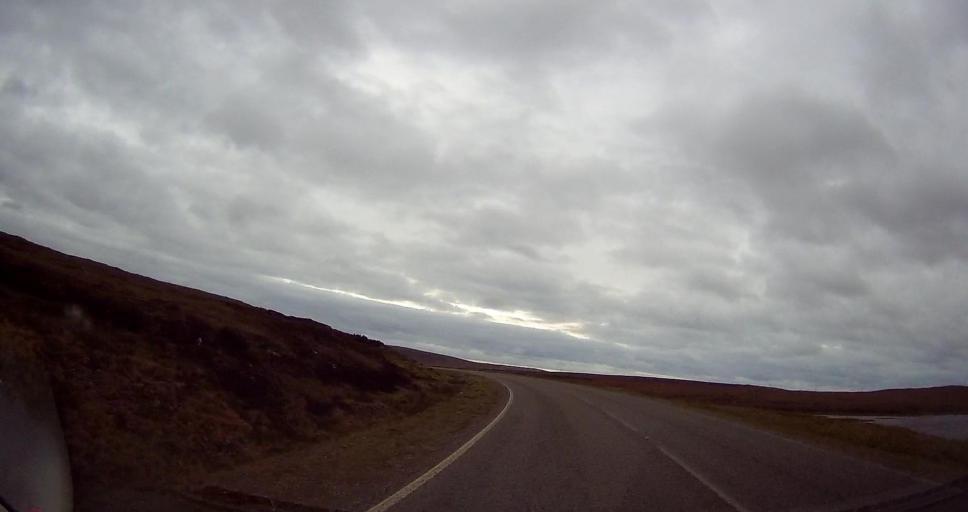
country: GB
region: Scotland
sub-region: Shetland Islands
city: Shetland
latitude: 60.6656
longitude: -1.0305
